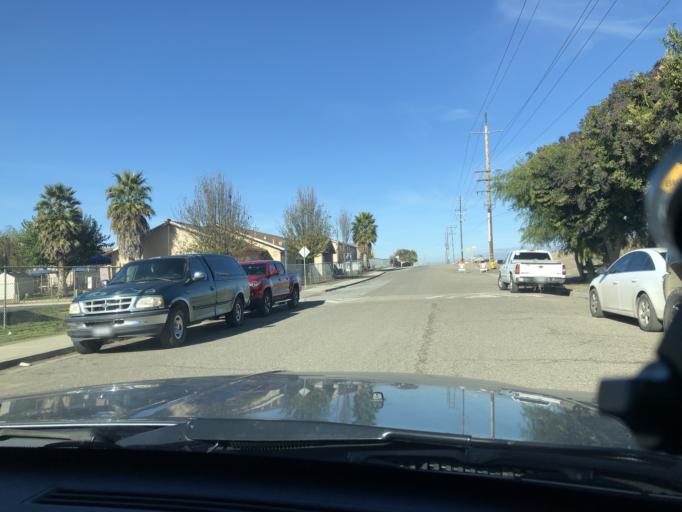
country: US
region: California
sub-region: Monterey County
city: King City
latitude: 36.2108
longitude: -121.1187
